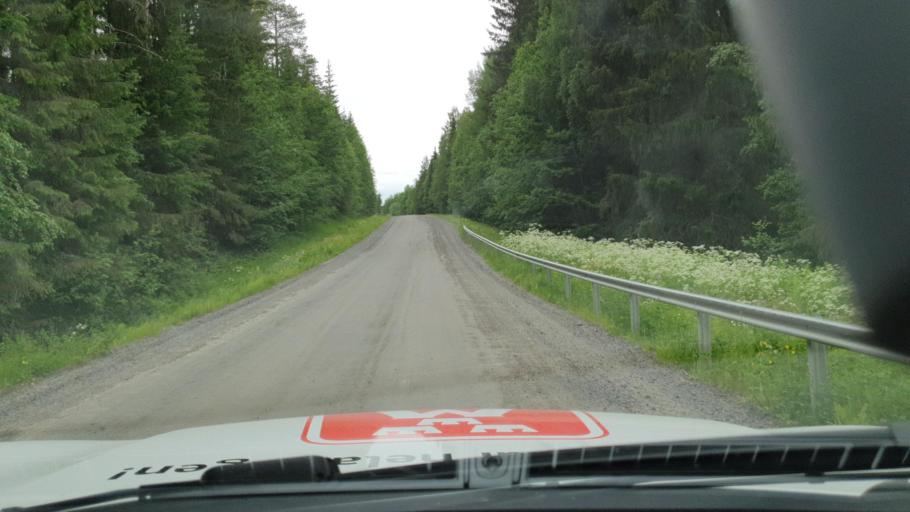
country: SE
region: Vaesterbotten
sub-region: Bjurholms Kommun
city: Bjurholm
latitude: 63.7934
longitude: 19.3595
